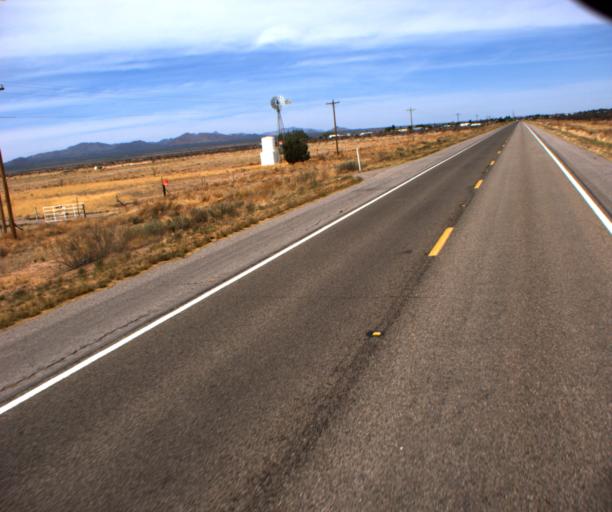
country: US
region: Arizona
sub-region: Cochise County
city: Pirtleville
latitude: 31.6612
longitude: -109.6782
